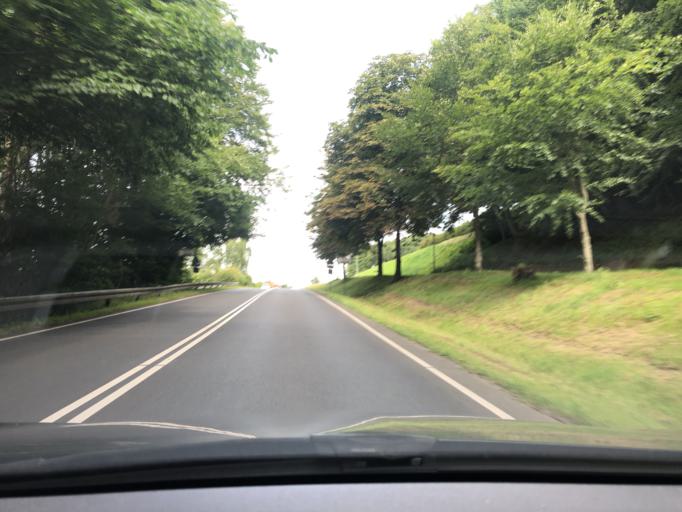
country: DK
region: South Denmark
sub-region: Vejle Kommune
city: Vejle
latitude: 55.6973
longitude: 9.4979
